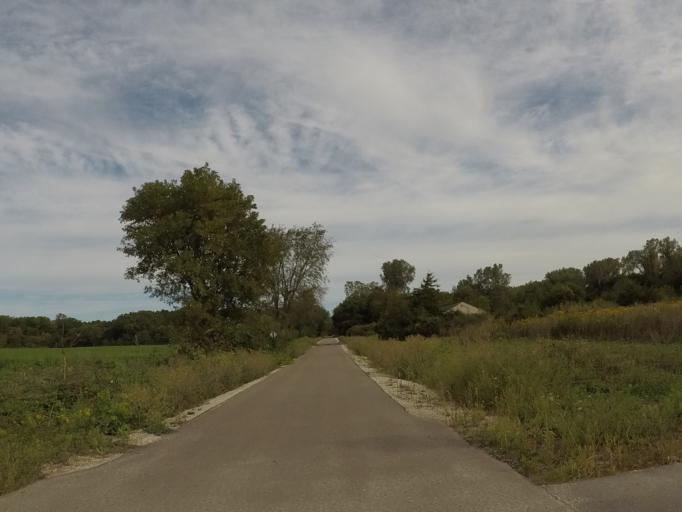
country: US
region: Wisconsin
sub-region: Sauk County
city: Prairie du Sac
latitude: 43.3510
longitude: -89.7406
